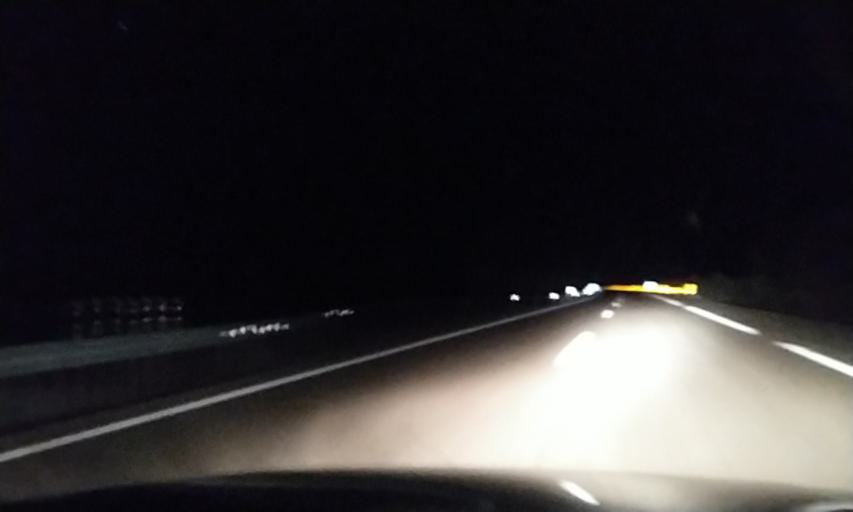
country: ES
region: Castille and Leon
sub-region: Provincia de Zamora
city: Santibanez de Tera
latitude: 42.0144
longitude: -5.9512
